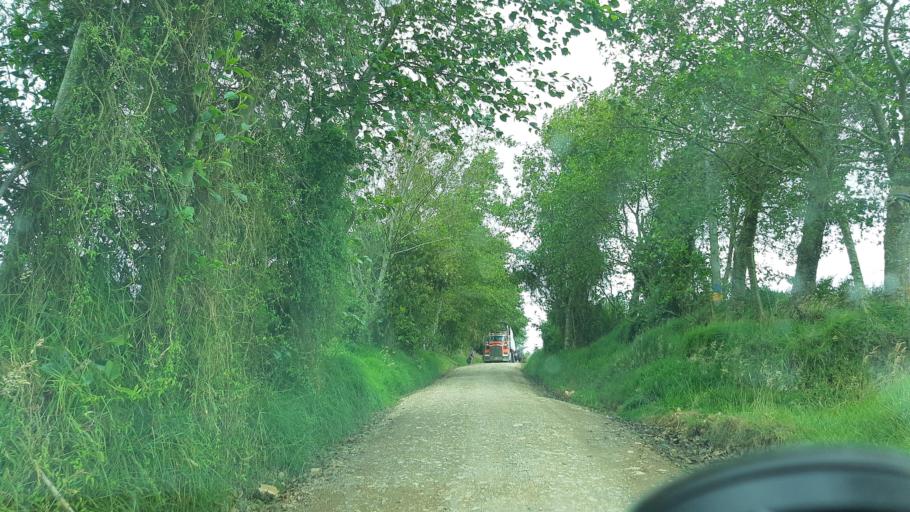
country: CO
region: Boyaca
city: Samaca
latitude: 5.4909
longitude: -73.4581
